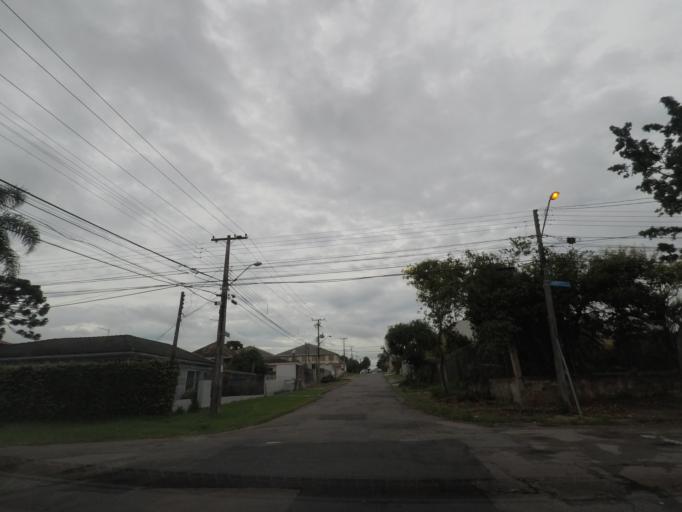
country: BR
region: Parana
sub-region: Curitiba
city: Curitiba
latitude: -25.4666
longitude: -49.3066
